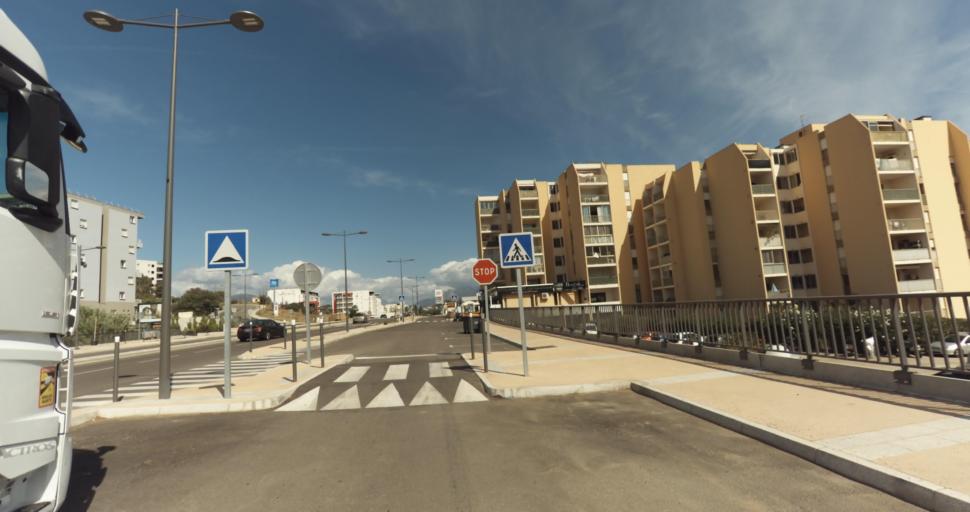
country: FR
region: Corsica
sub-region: Departement de la Corse-du-Sud
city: Ajaccio
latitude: 41.9431
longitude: 8.7534
